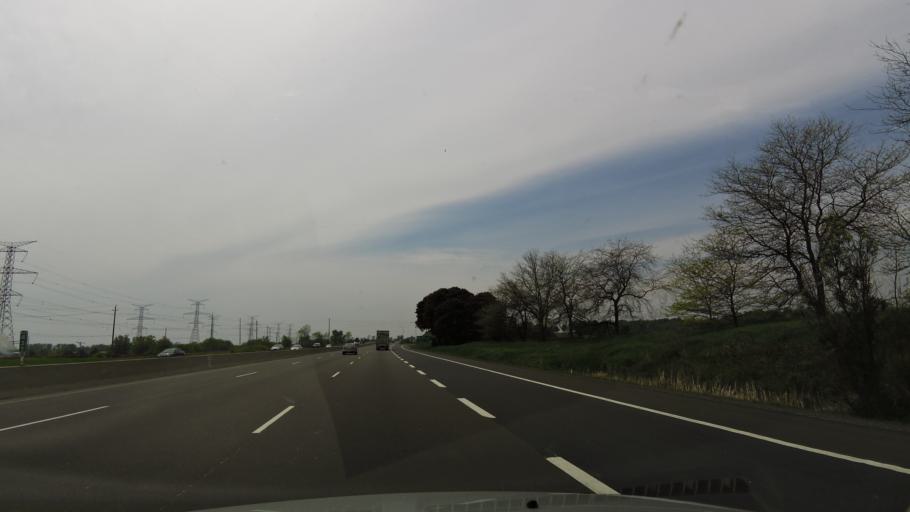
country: CA
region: Ontario
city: Oshawa
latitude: 43.9038
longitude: -78.6193
